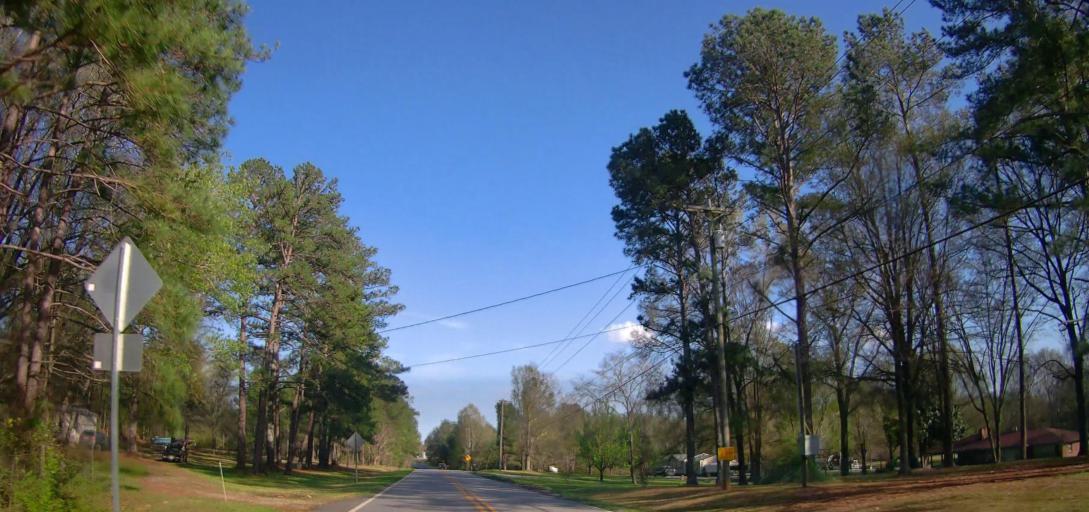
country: US
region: Georgia
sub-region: Putnam County
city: Eatonton
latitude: 33.1974
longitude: -83.4003
